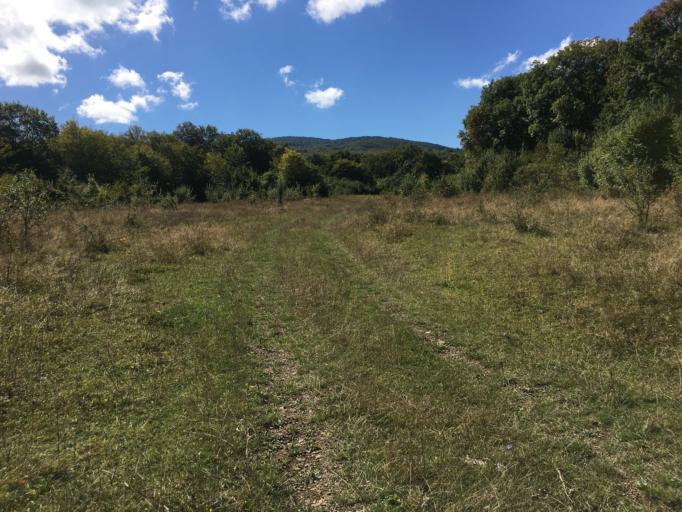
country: GE
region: Mtskheta-Mtianeti
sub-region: Tianetis Munitsip'alit'et'i
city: T'ianet'i
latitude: 41.9339
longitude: 44.9755
